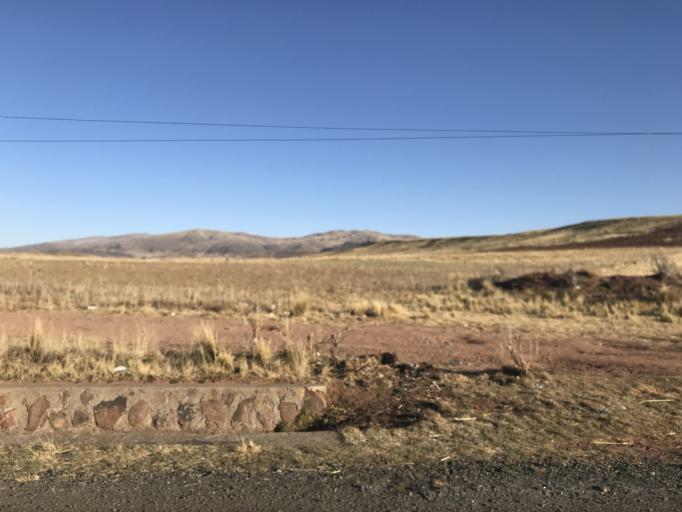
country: BO
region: La Paz
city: Tiahuanaco
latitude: -16.5658
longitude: -68.6424
